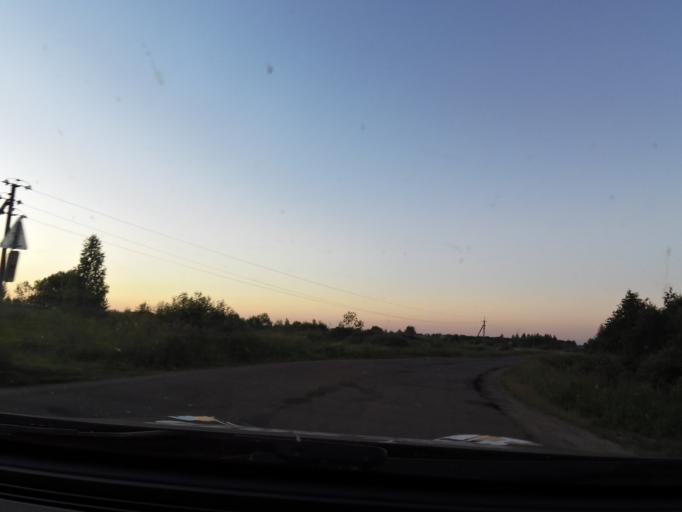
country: RU
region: Kostroma
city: Buy
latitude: 58.4086
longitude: 41.2406
